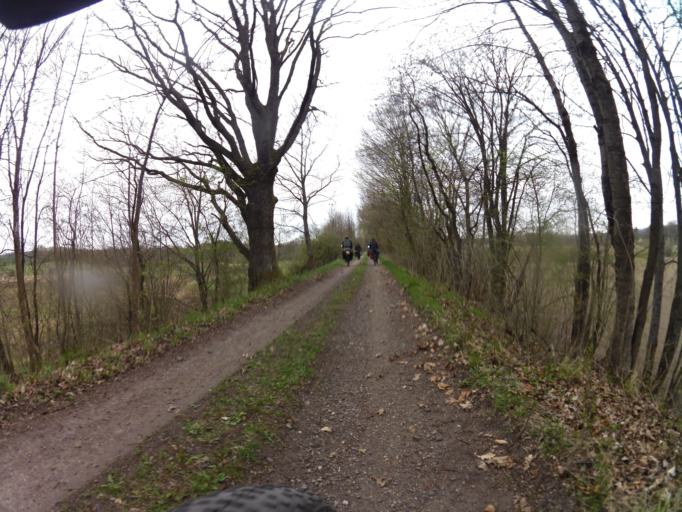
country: PL
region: West Pomeranian Voivodeship
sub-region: Powiat koszalinski
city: Bobolice
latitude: 54.0055
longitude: 16.6664
